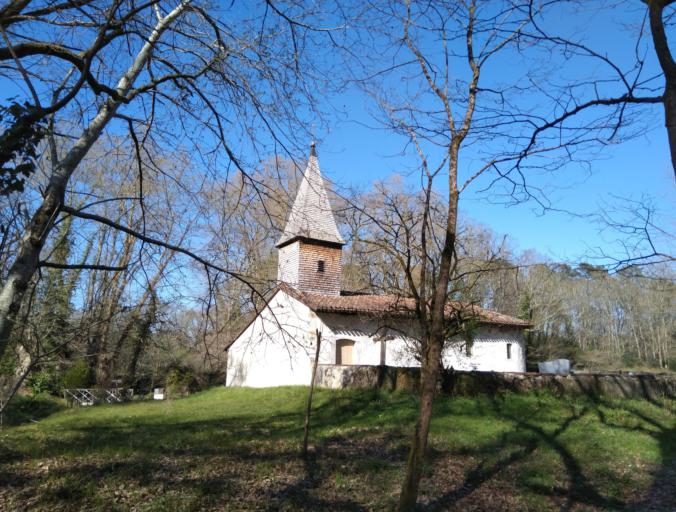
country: FR
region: Aquitaine
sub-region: Departement des Landes
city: Saint-Geours-de-Maremne
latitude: 43.7088
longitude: -1.1889
